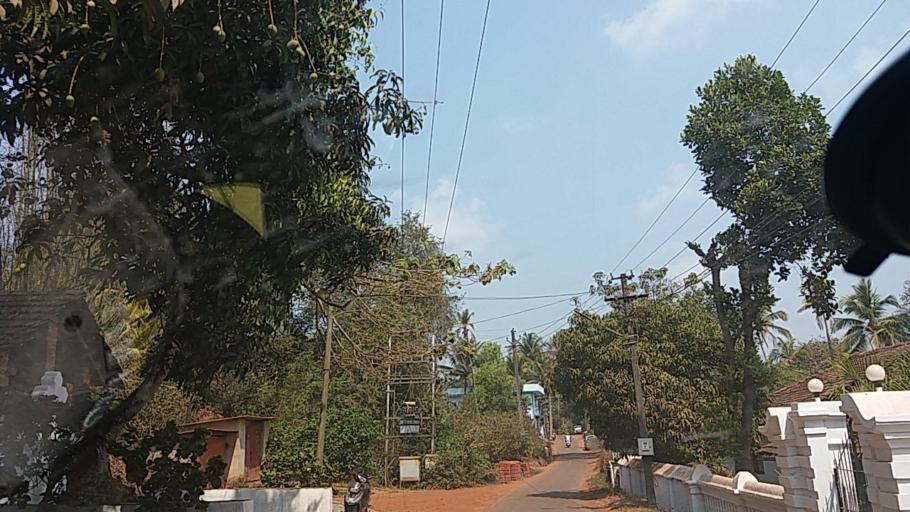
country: IN
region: Goa
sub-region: South Goa
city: Sancoale
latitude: 15.3703
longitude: 73.9153
